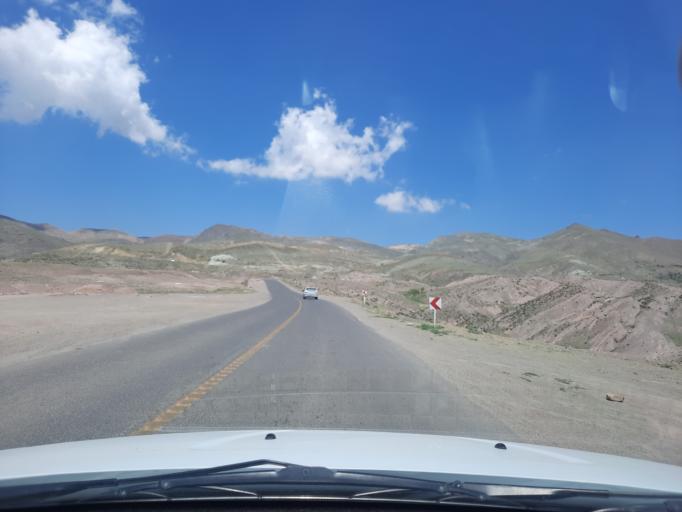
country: IR
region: Qazvin
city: Qazvin
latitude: 36.3489
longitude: 50.1861
